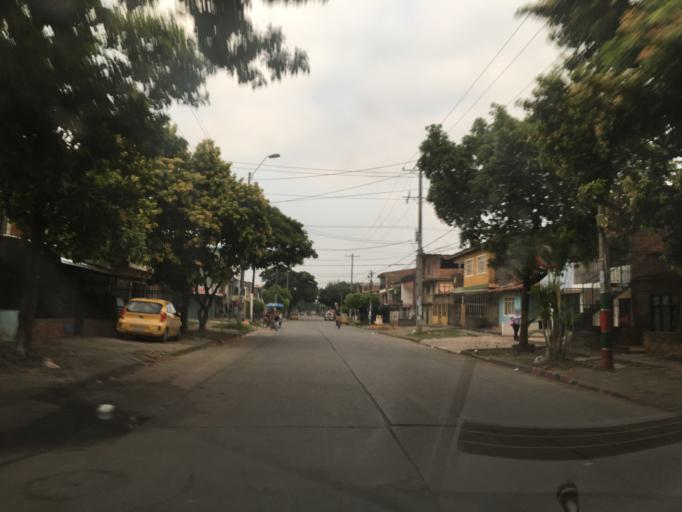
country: CO
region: Valle del Cauca
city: Cali
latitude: 3.4169
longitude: -76.5222
